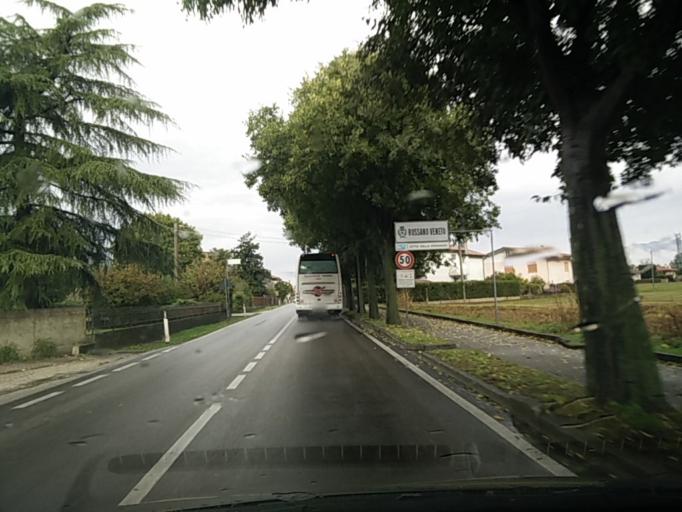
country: IT
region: Veneto
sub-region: Provincia di Vicenza
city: Rossano Veneto
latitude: 45.7024
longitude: 11.8178
